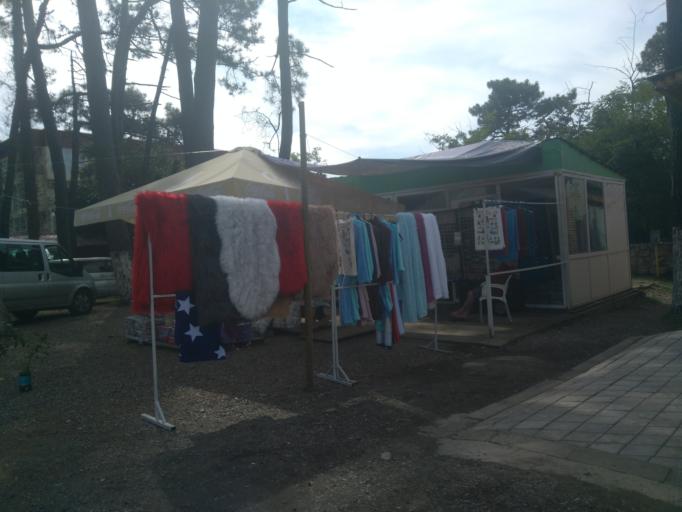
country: GE
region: Guria
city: Urek'i
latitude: 41.9975
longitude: 41.7599
